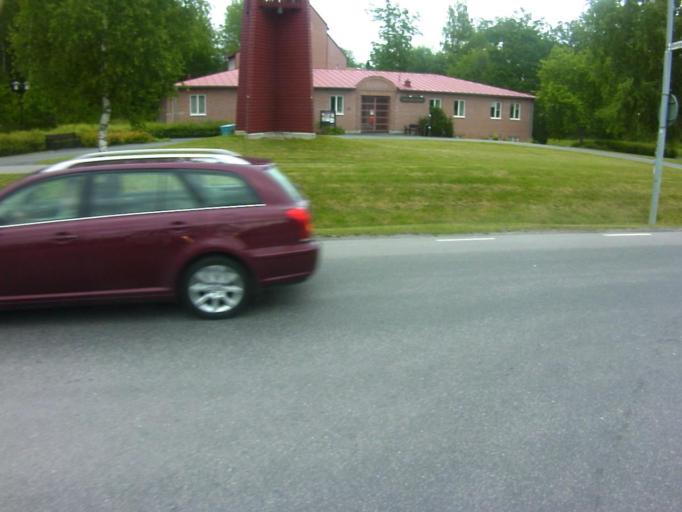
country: SE
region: Soedermanland
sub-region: Eskilstuna Kommun
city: Skogstorp
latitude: 59.3565
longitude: 16.4769
